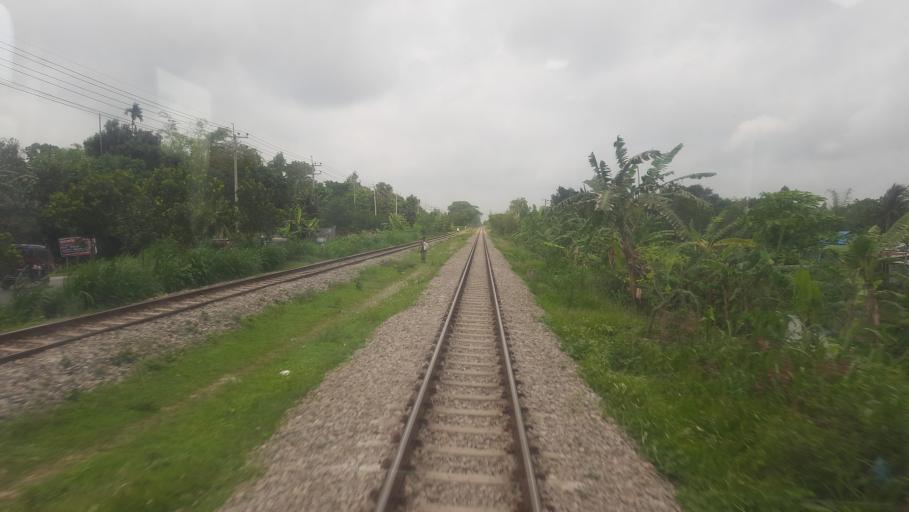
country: BD
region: Dhaka
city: Narsingdi
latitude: 23.9319
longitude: 90.7456
